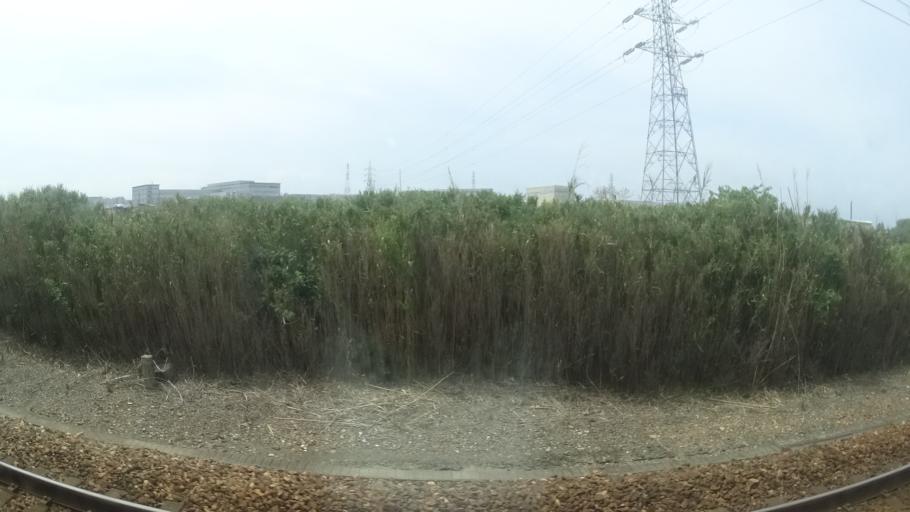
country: JP
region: Shizuoka
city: Kosai-shi
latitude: 34.7241
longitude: 137.4804
